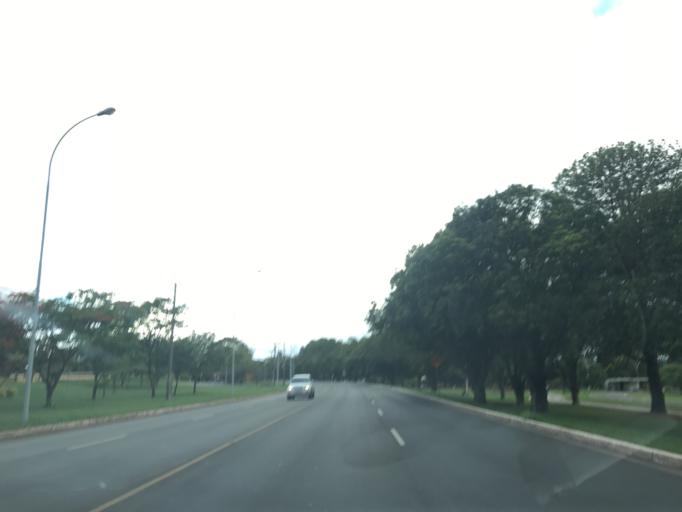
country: BR
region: Federal District
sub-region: Brasilia
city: Brasilia
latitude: -15.8054
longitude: -47.9227
